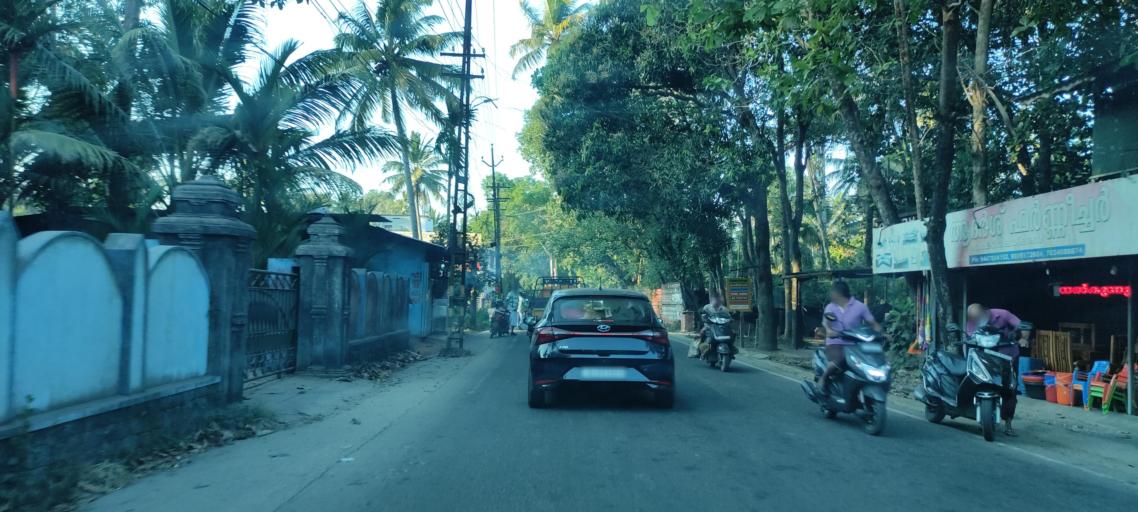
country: IN
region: Kerala
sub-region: Alappuzha
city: Kayankulam
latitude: 9.1763
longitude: 76.4790
